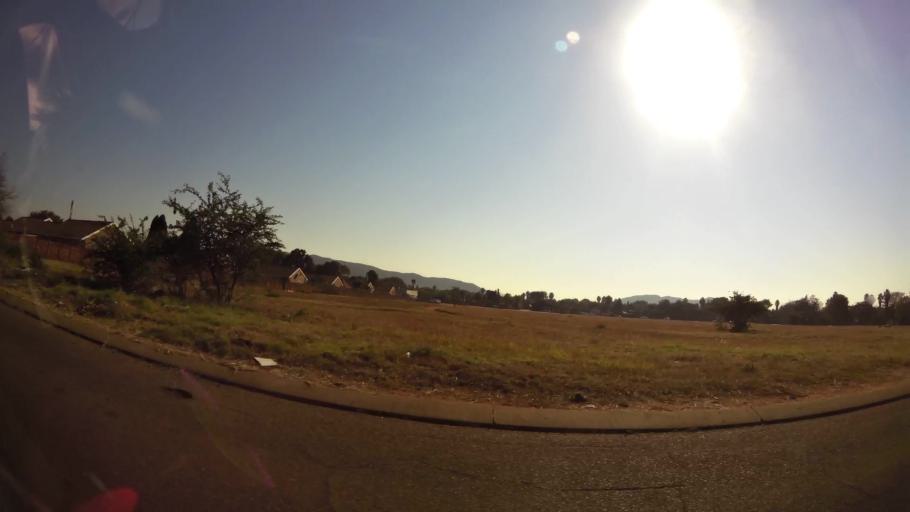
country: ZA
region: Gauteng
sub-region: City of Tshwane Metropolitan Municipality
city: Pretoria
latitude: -25.6508
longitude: 28.2378
